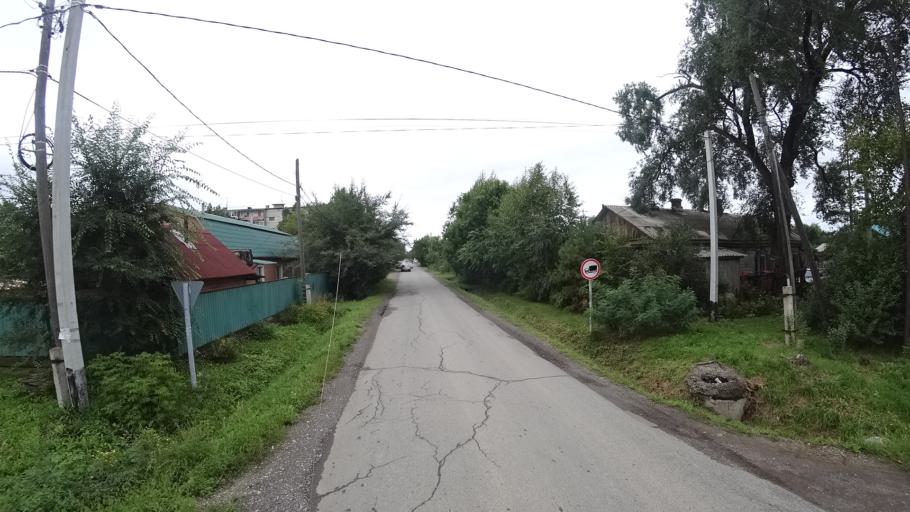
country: RU
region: Primorskiy
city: Chernigovka
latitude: 44.3464
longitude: 132.5747
